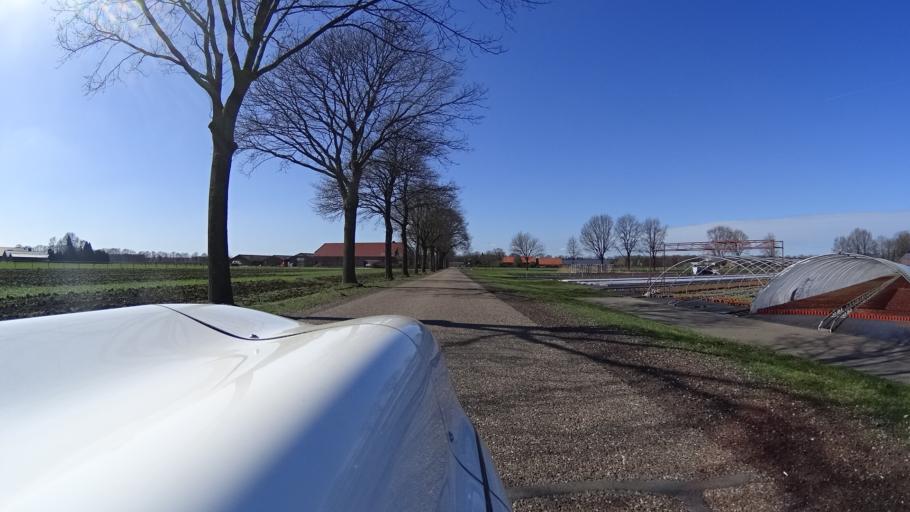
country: NL
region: Limburg
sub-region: Gemeente Venray
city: Venray
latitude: 51.5631
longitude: 6.0038
